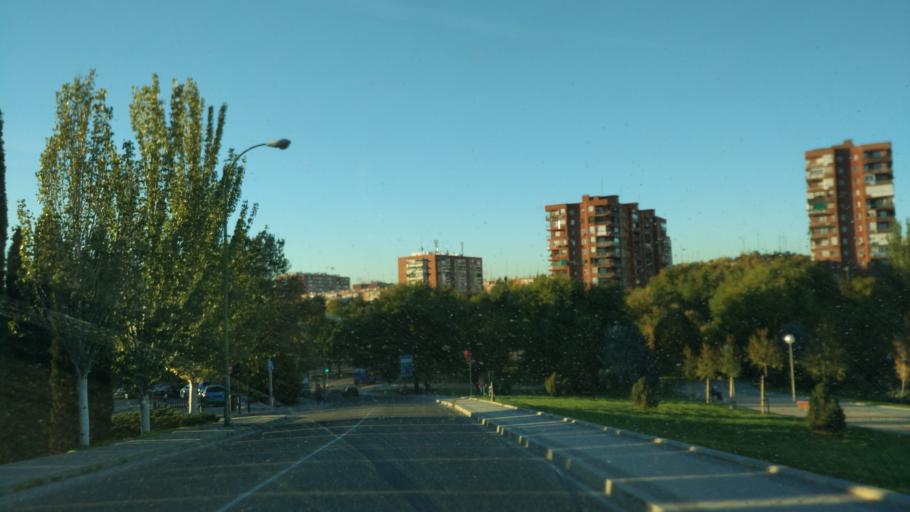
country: ES
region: Madrid
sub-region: Provincia de Madrid
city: Tetuan de las Victorias
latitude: 40.4697
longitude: -3.7103
